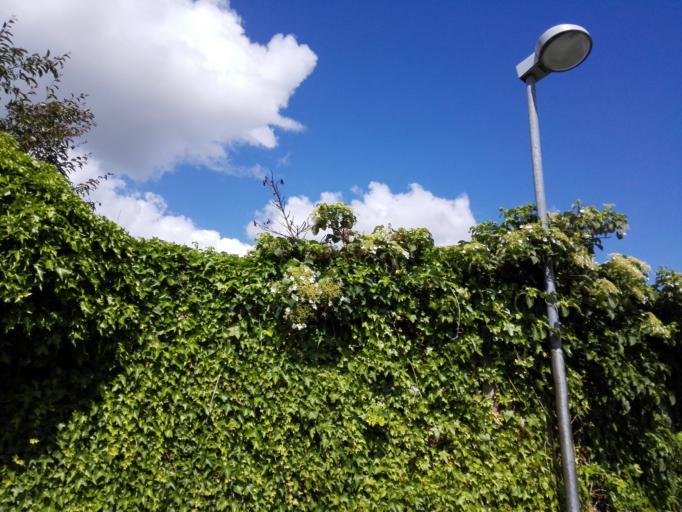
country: DK
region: Capital Region
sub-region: Allerod Kommune
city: Lynge
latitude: 55.8390
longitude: 12.2707
